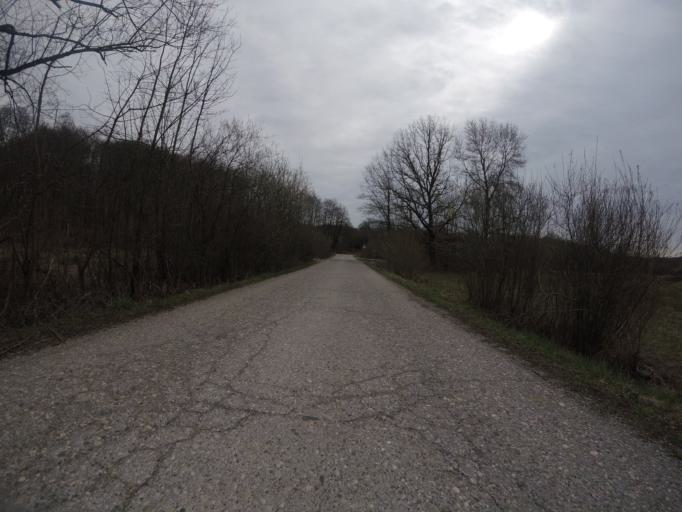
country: HR
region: Grad Zagreb
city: Strmec
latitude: 45.5946
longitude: 15.9169
